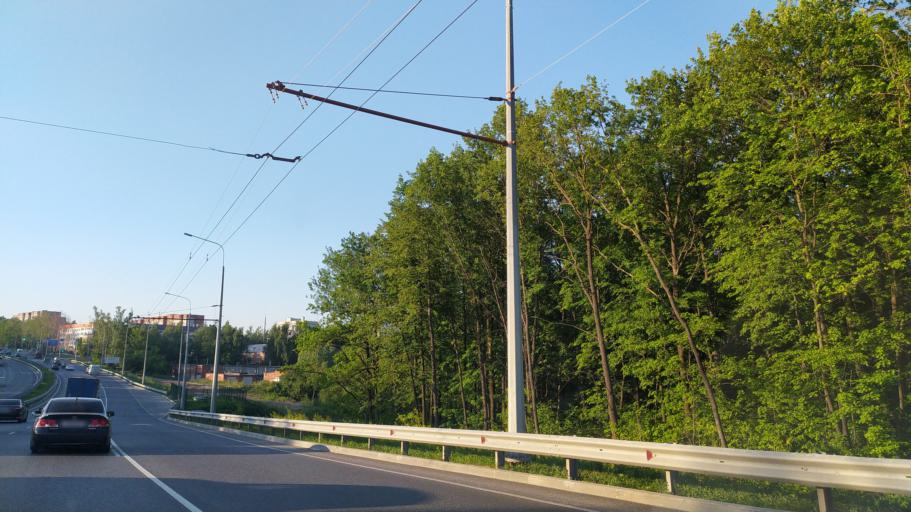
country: RU
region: Chuvashia
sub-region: Cheboksarskiy Rayon
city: Cheboksary
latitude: 56.0833
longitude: 47.2674
